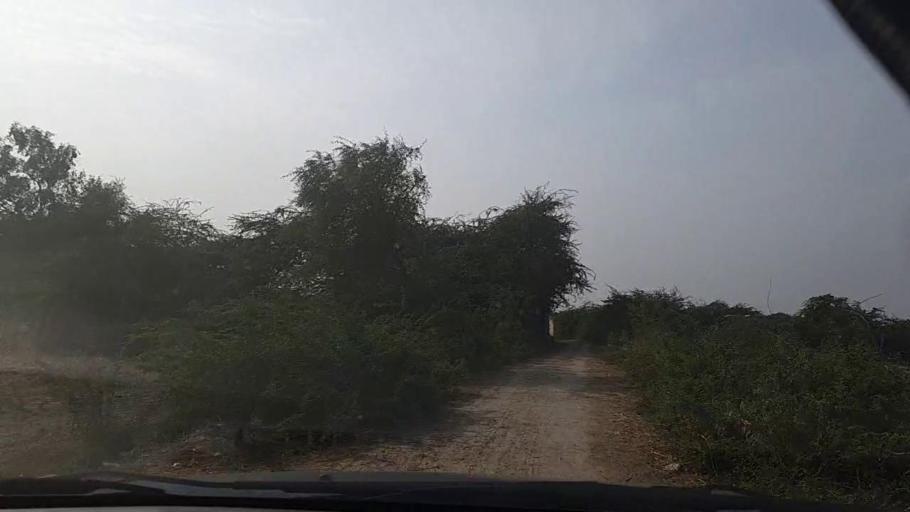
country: PK
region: Sindh
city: Thatta
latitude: 24.6173
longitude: 67.9510
